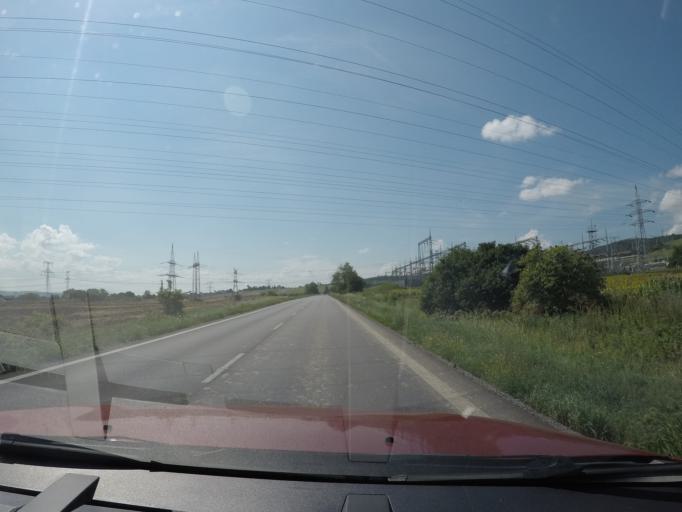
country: SK
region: Presovsky
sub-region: Okres Presov
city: Presov
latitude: 48.8625
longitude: 21.2561
